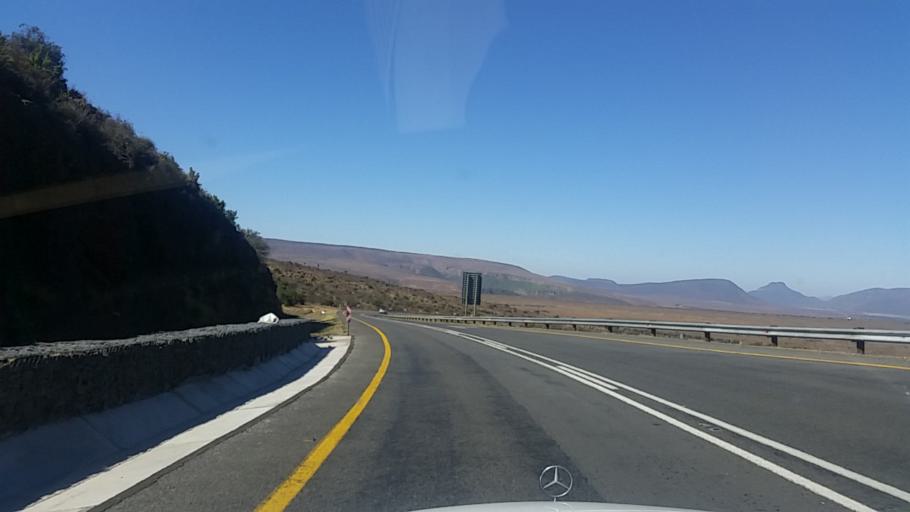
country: ZA
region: Eastern Cape
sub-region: Cacadu District Municipality
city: Graaff-Reinet
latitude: -32.1146
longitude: 24.6083
